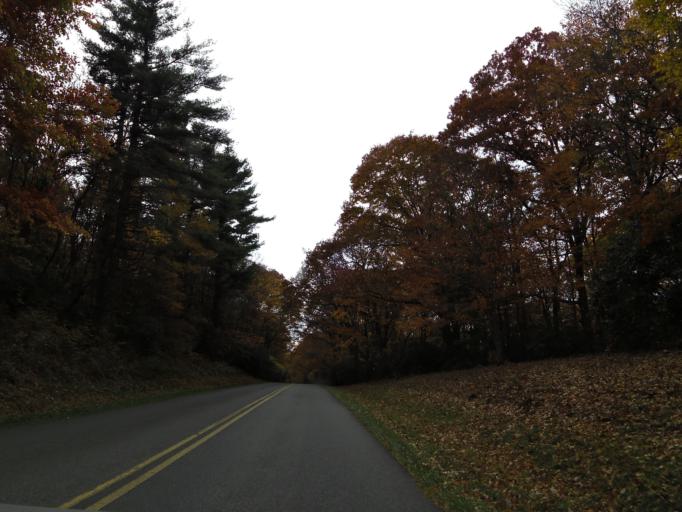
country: US
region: Virginia
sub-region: Carroll County
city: Cana
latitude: 36.6493
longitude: -80.7206
